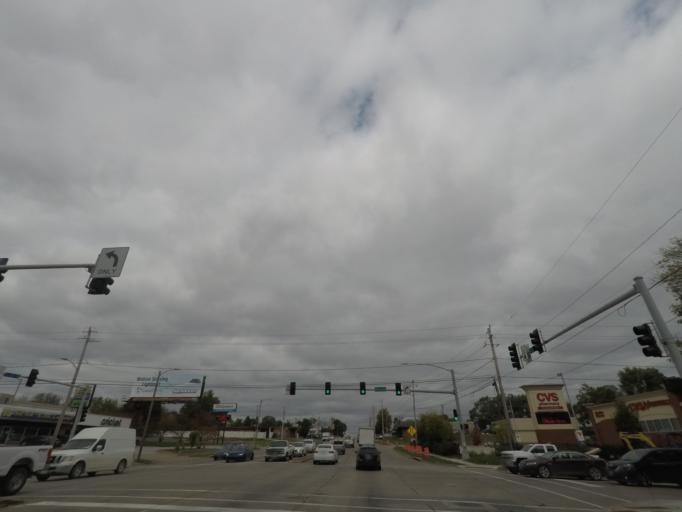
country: US
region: Iowa
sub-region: Polk County
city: Des Moines
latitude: 41.5551
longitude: -93.5967
